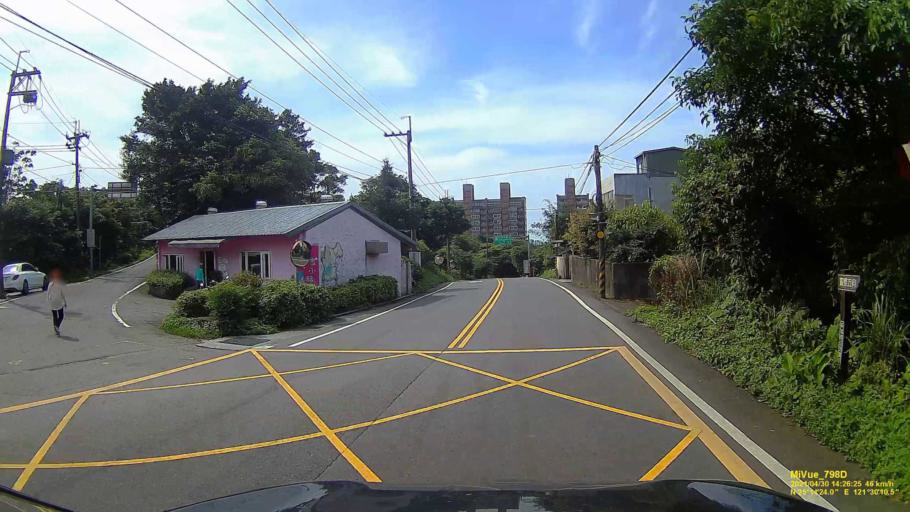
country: TW
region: Taipei
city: Taipei
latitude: 25.2403
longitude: 121.5028
